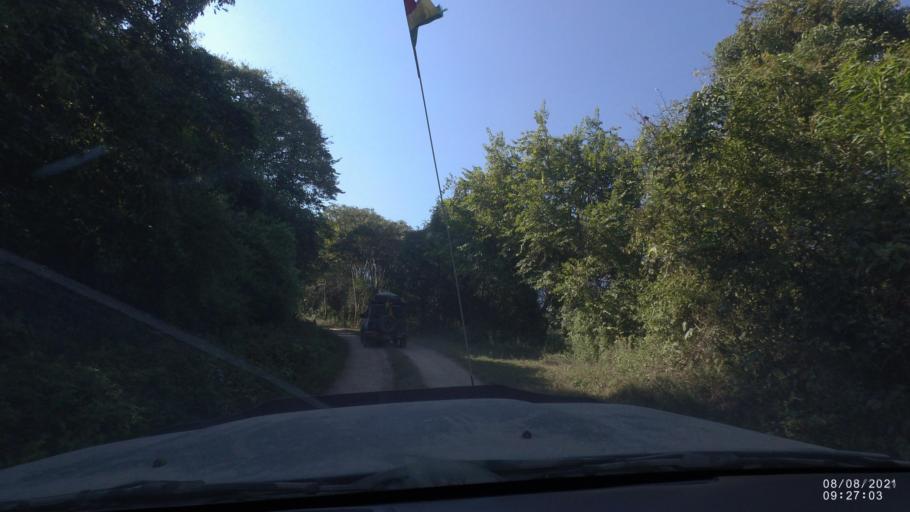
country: BO
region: La Paz
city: Quime
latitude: -16.5899
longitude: -66.7209
